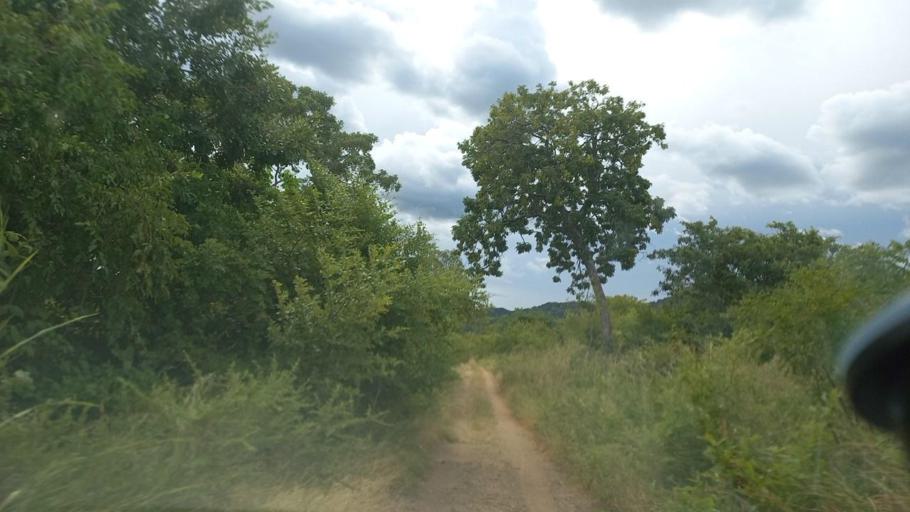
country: ZM
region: Lusaka
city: Luangwa
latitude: -15.6495
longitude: 30.3397
